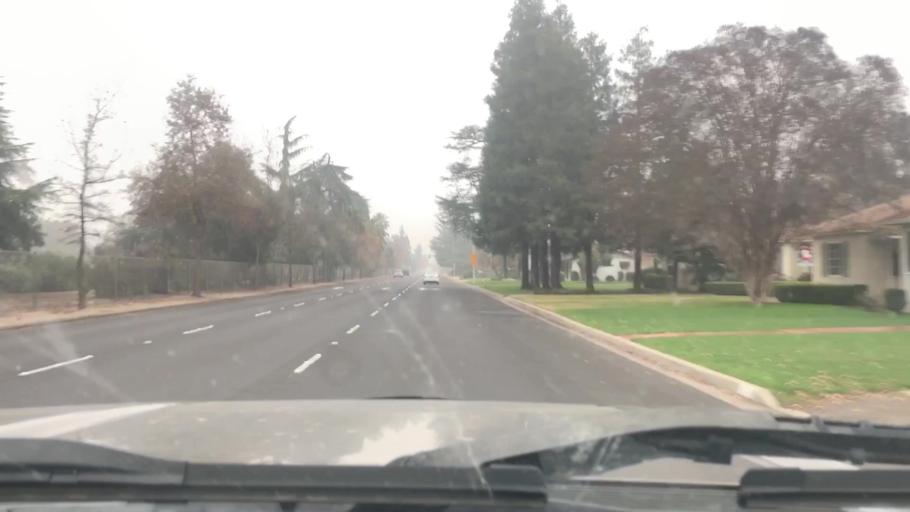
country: US
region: California
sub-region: Tulare County
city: Visalia
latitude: 36.3265
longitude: -119.3088
